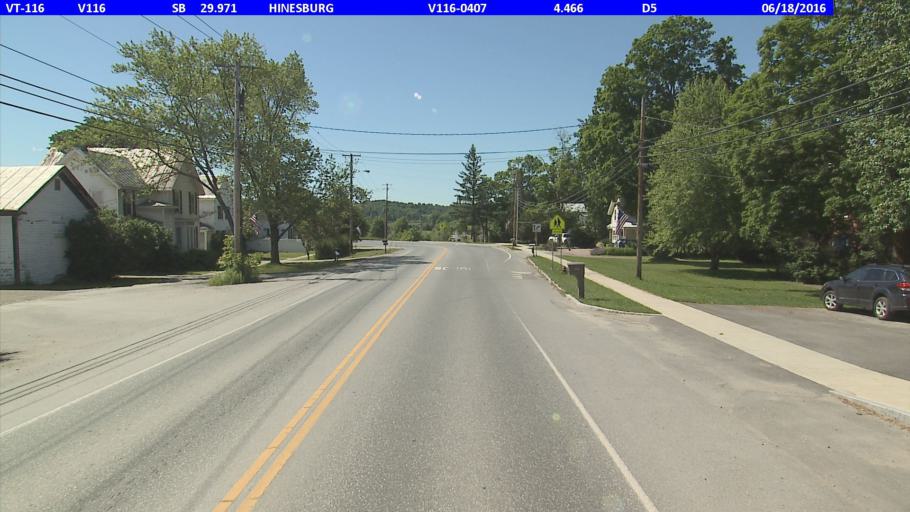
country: US
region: Vermont
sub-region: Chittenden County
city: Hinesburg
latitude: 44.3278
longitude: -73.1101
